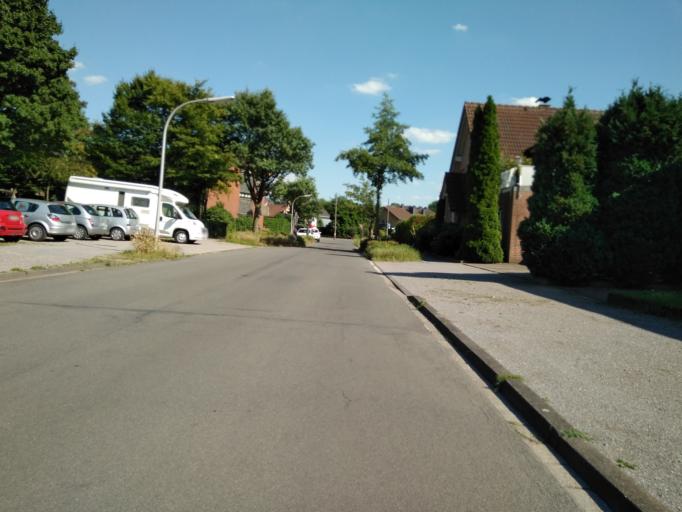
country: DE
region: North Rhine-Westphalia
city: Dorsten
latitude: 51.6753
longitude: 6.9479
